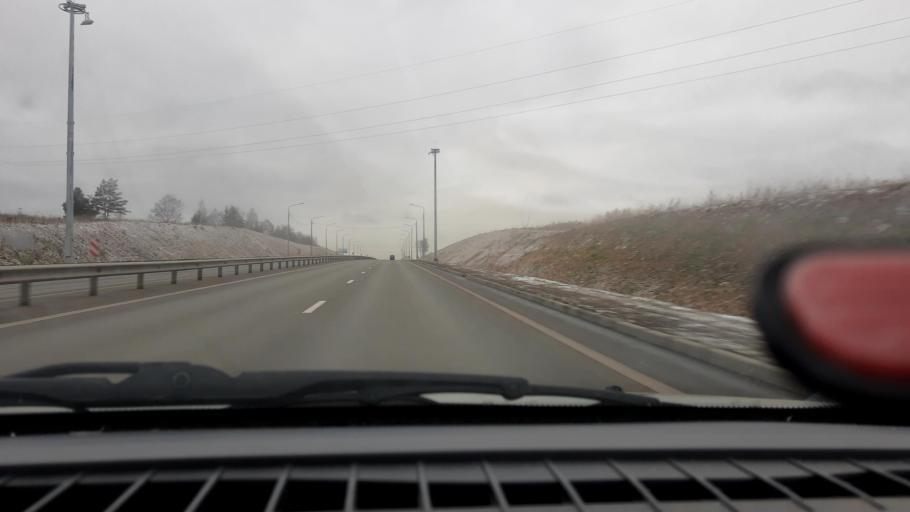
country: RU
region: Nizjnij Novgorod
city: Burevestnik
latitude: 56.0951
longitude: 43.9187
